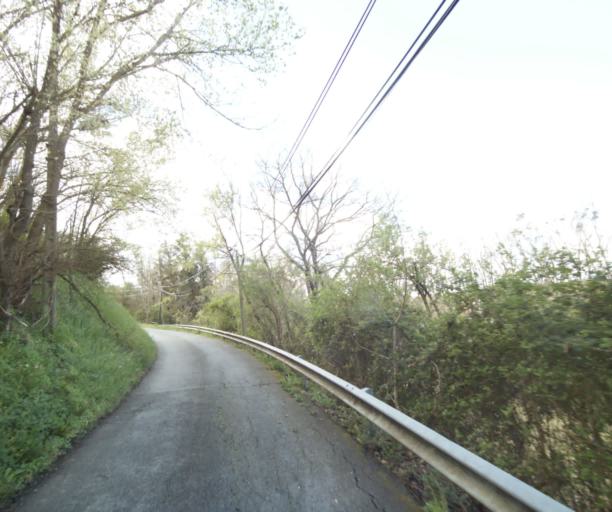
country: FR
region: Midi-Pyrenees
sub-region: Departement de l'Ariege
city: Saverdun
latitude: 43.2303
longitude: 1.5761
